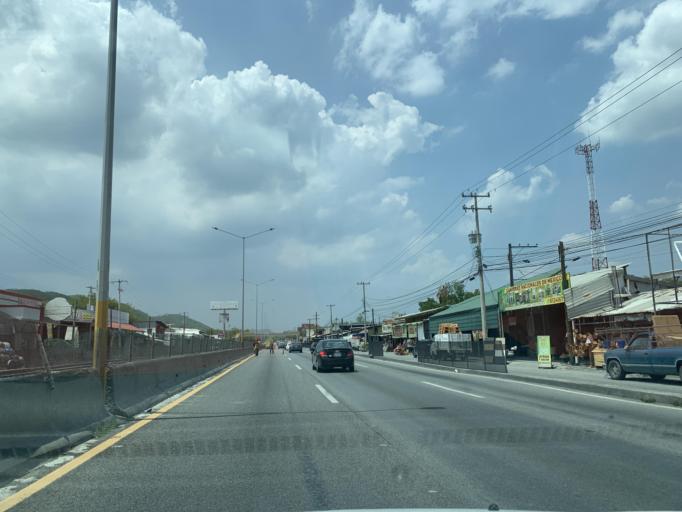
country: MX
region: Nuevo Leon
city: Santiago
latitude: 25.4524
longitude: -100.1635
